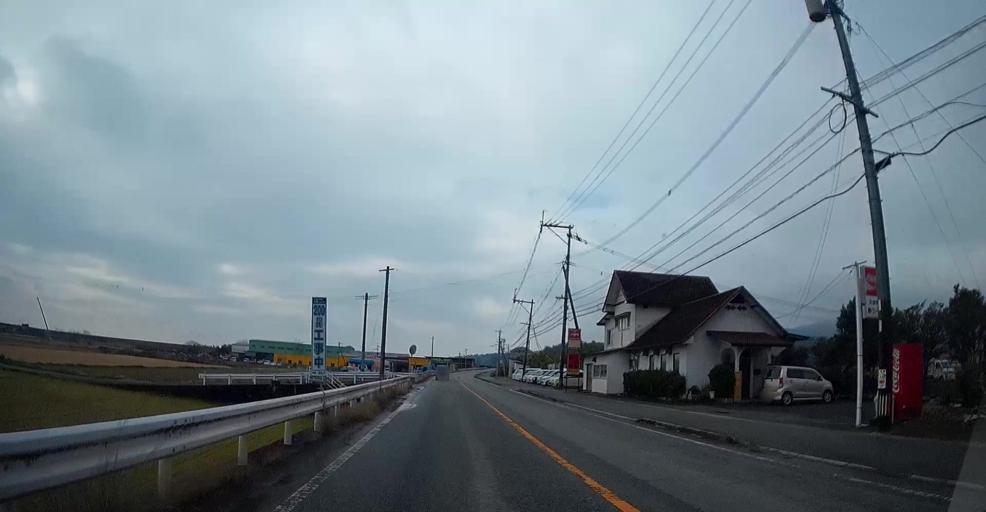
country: JP
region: Kumamoto
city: Matsubase
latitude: 32.6438
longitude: 130.6543
